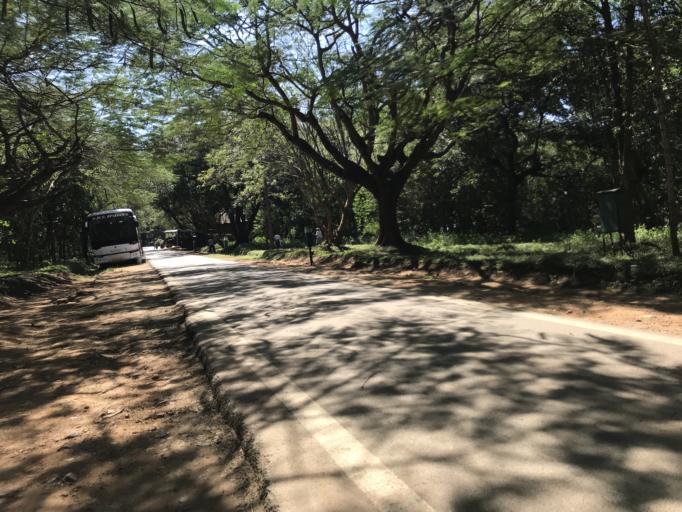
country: IN
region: Karnataka
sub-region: Mysore
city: Sargur
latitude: 11.9410
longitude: 76.2691
